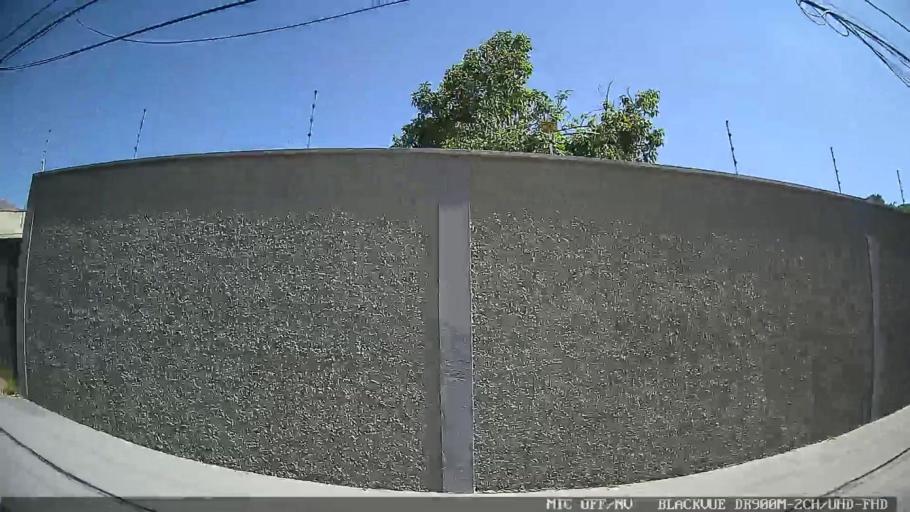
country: BR
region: Sao Paulo
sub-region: Peruibe
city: Peruibe
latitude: -24.2919
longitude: -46.9735
